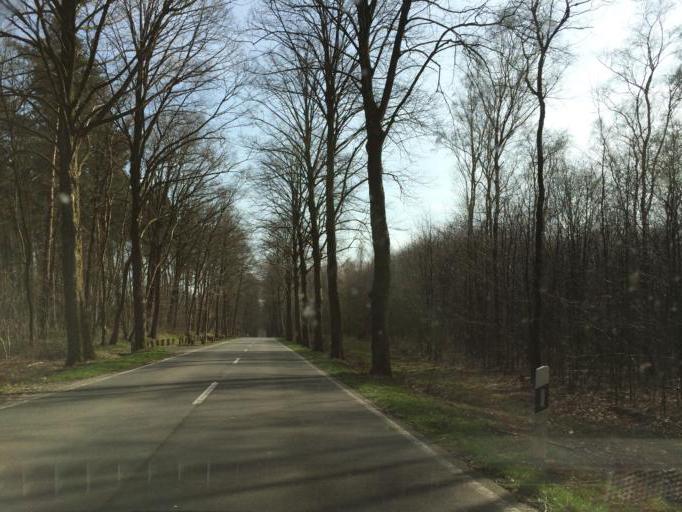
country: DE
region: North Rhine-Westphalia
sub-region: Regierungsbezirk Munster
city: Klein Reken
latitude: 51.7677
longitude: 7.1085
